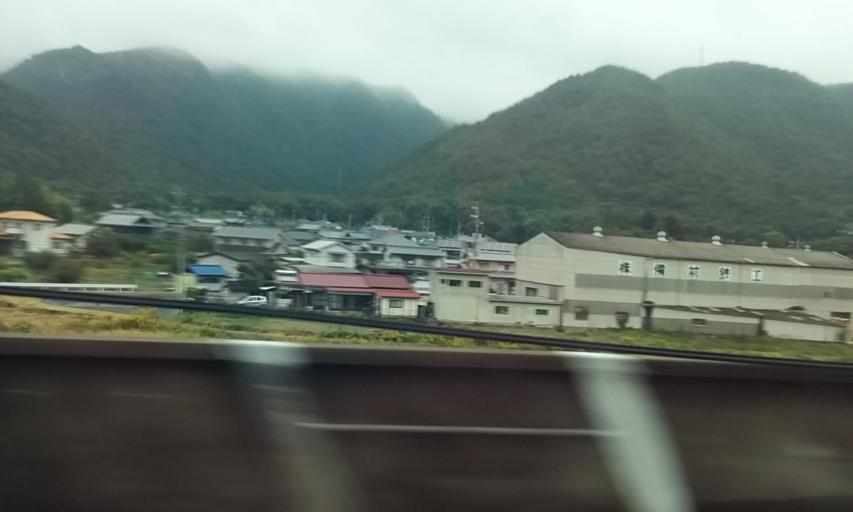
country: JP
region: Okayama
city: Okayama-shi
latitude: 34.7339
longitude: 134.1367
